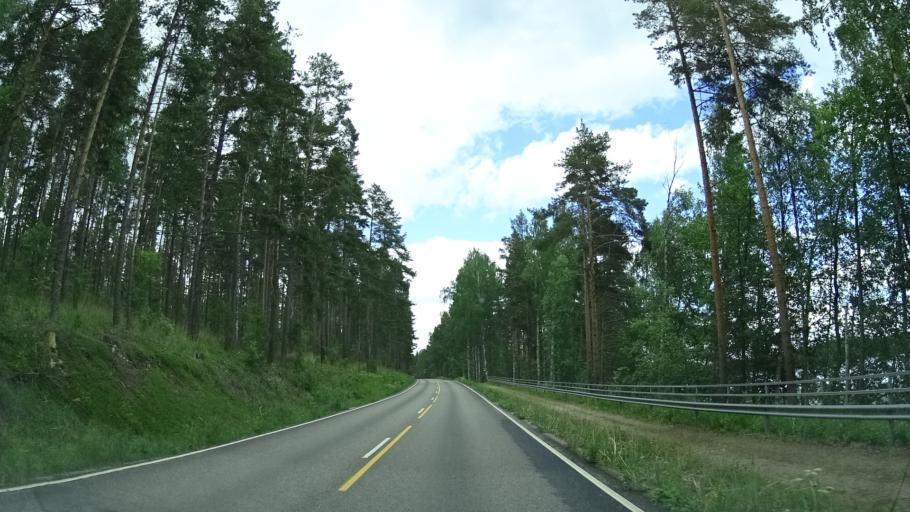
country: FI
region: Paijanne Tavastia
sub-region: Lahti
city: Asikkala
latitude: 61.3056
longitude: 25.5434
